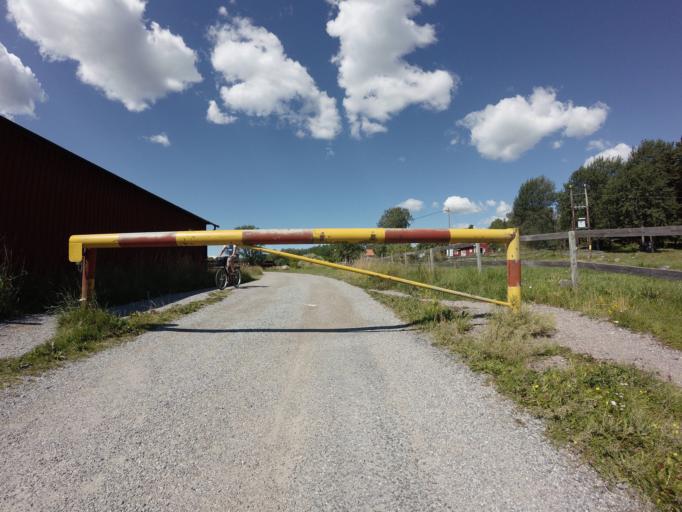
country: SE
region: Stockholm
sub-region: Jarfalla Kommun
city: Jakobsberg
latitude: 59.4636
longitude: 17.8698
